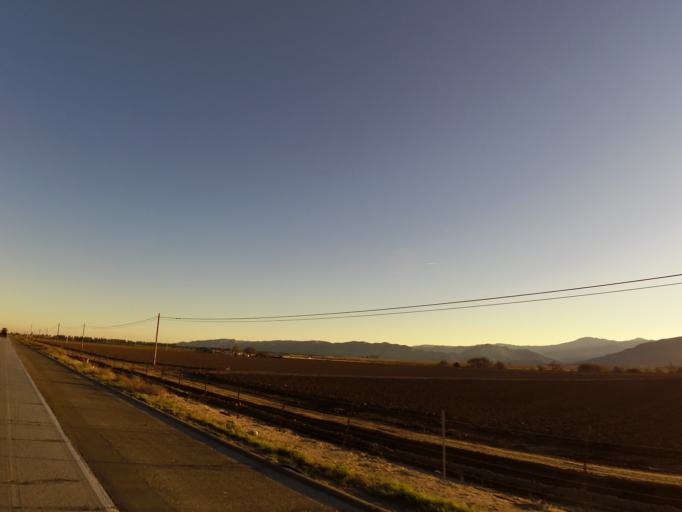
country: US
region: California
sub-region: Monterey County
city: Soledad
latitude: 36.3732
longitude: -121.2890
